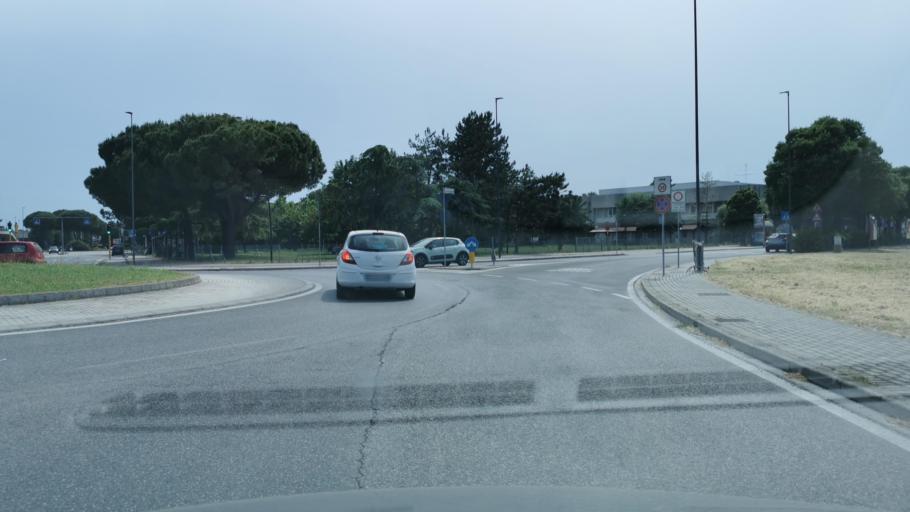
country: IT
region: Emilia-Romagna
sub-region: Provincia di Ravenna
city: Ravenna
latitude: 44.4252
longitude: 12.1825
